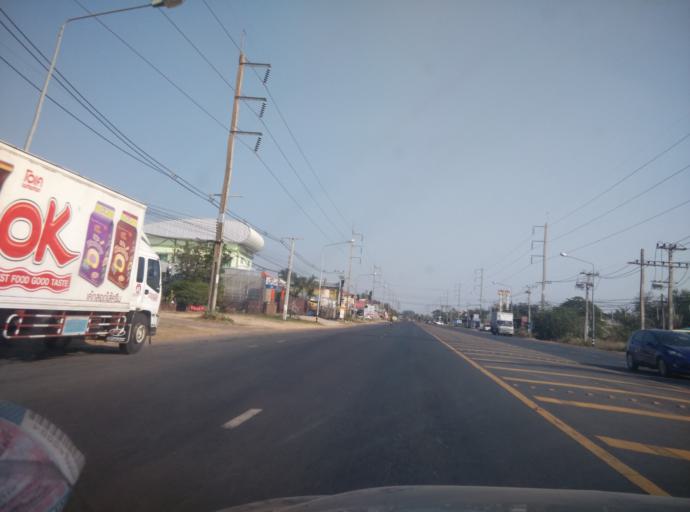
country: TH
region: Sisaket
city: Uthumphon Phisai
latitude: 15.1655
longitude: 104.1601
